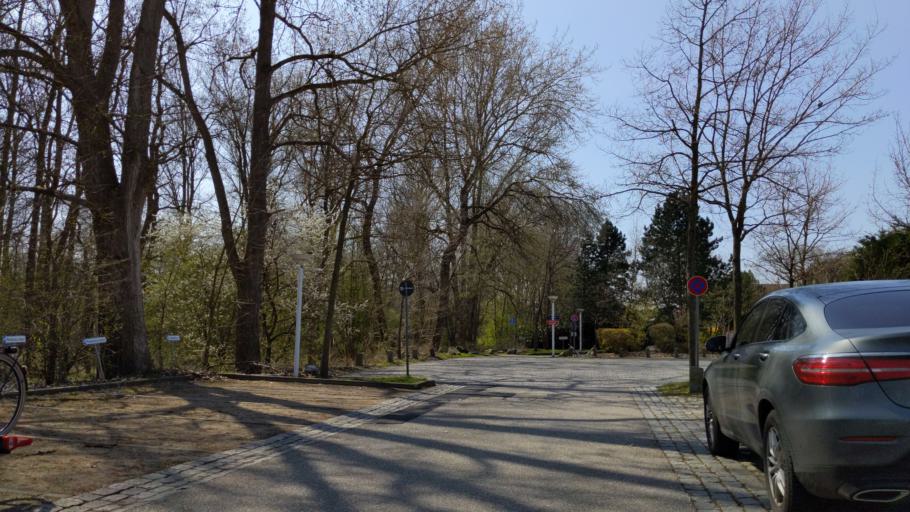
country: DE
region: Schleswig-Holstein
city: Travemuende
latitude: 53.9520
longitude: 10.8701
